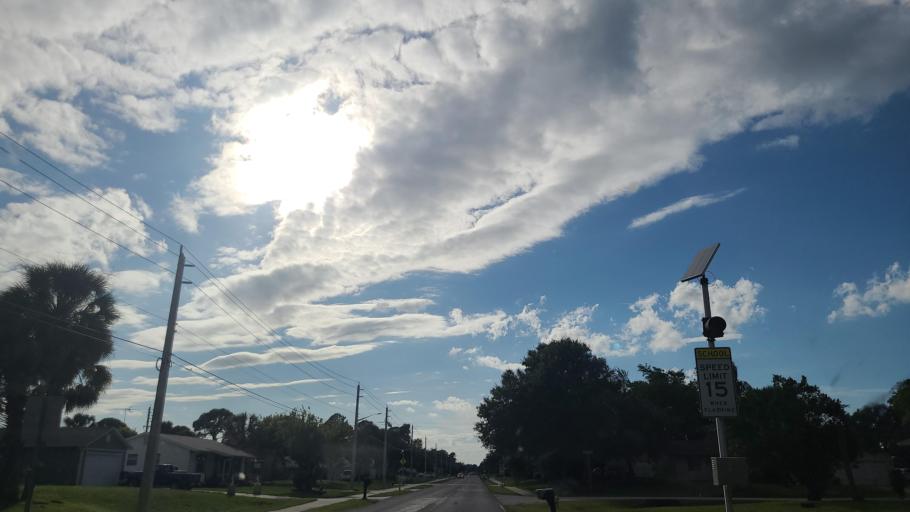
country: US
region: Florida
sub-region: Brevard County
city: June Park
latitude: 28.0108
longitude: -80.6738
